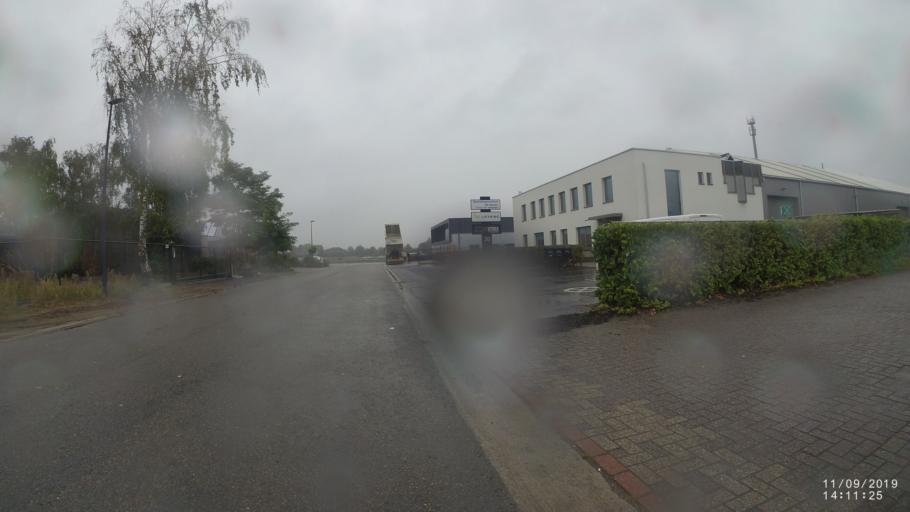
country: BE
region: Flanders
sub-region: Provincie Oost-Vlaanderen
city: Evergem
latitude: 51.0891
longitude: 3.6741
